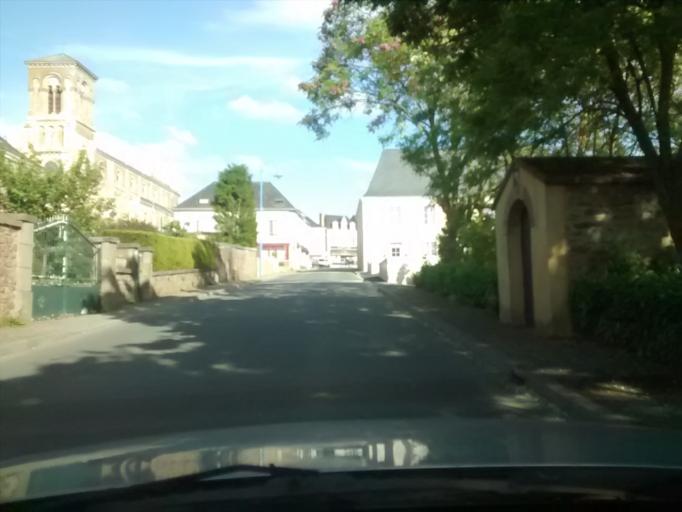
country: FR
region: Pays de la Loire
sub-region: Departement de la Mayenne
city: Entrammes
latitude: 47.9222
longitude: -0.6780
